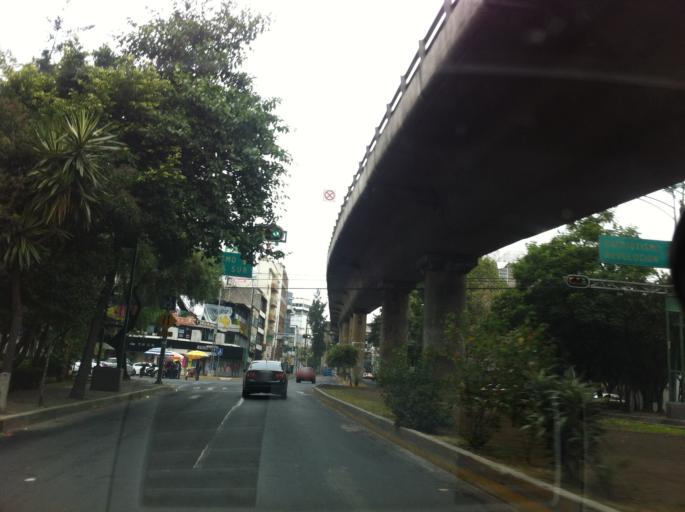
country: MX
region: Mexico City
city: Colonia del Valle
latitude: 19.3853
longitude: -99.1801
